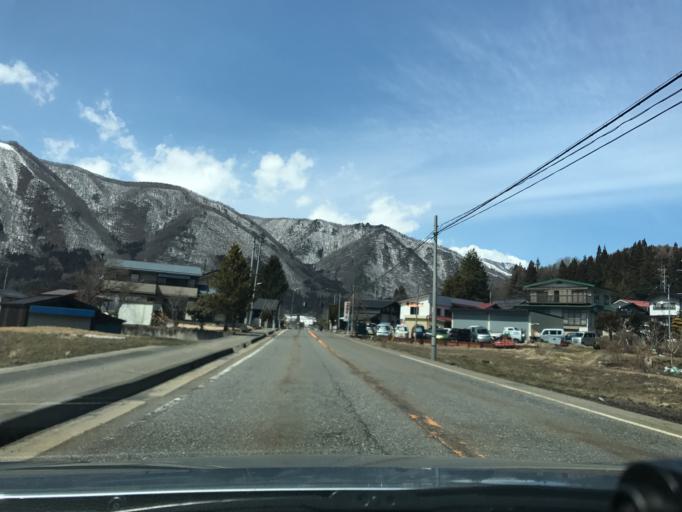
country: JP
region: Nagano
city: Omachi
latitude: 36.5647
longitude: 137.8431
